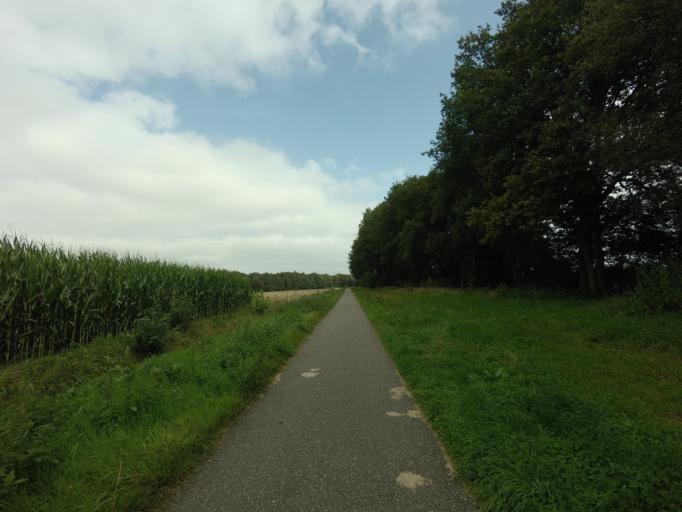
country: NL
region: Drenthe
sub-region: Gemeente Westerveld
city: Havelte
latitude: 52.8674
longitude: 6.2719
